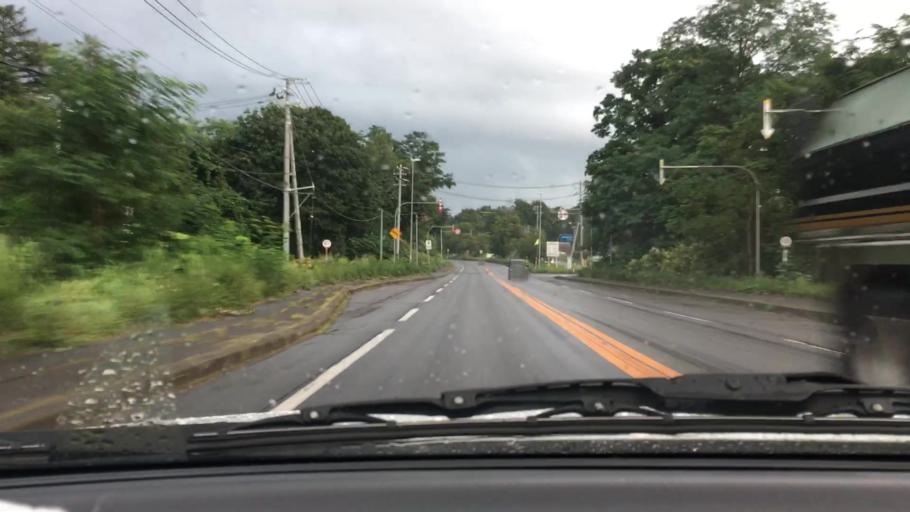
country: JP
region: Hokkaido
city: Nanae
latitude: 42.0846
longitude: 140.5852
